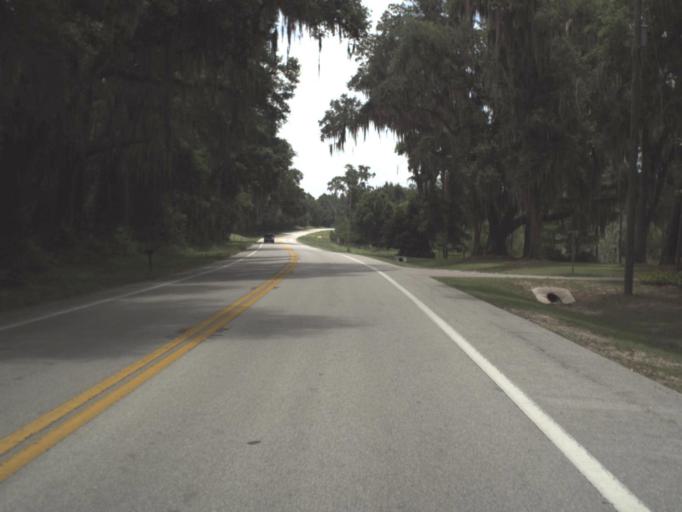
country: US
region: Florida
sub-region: Madison County
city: Madison
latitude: 30.4992
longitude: -83.4226
